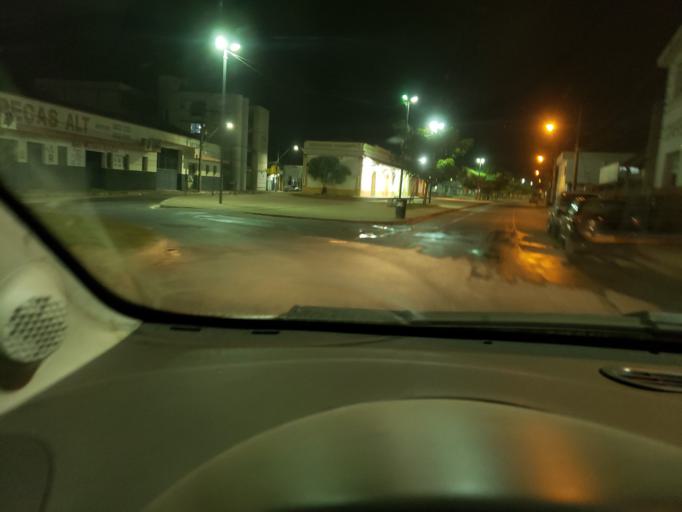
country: BR
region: Minas Gerais
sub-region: Campo Belo
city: Campo Belo
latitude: -20.8937
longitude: -45.2710
